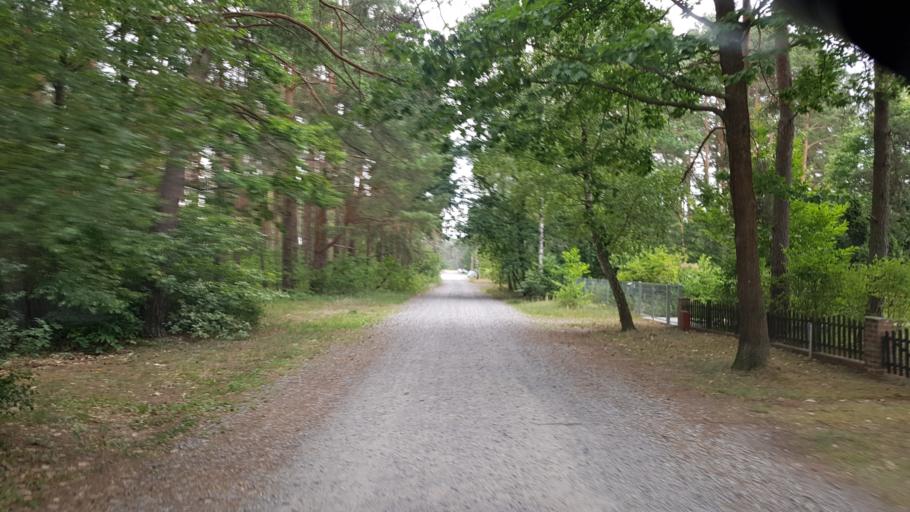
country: DE
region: Brandenburg
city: Gross Koris
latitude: 52.1629
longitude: 13.6968
